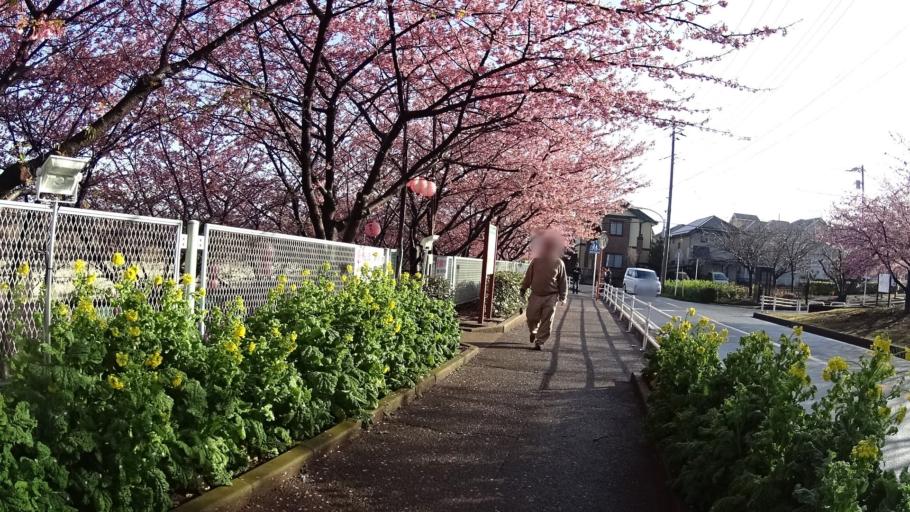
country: JP
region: Kanagawa
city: Miura
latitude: 35.1828
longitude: 139.6422
